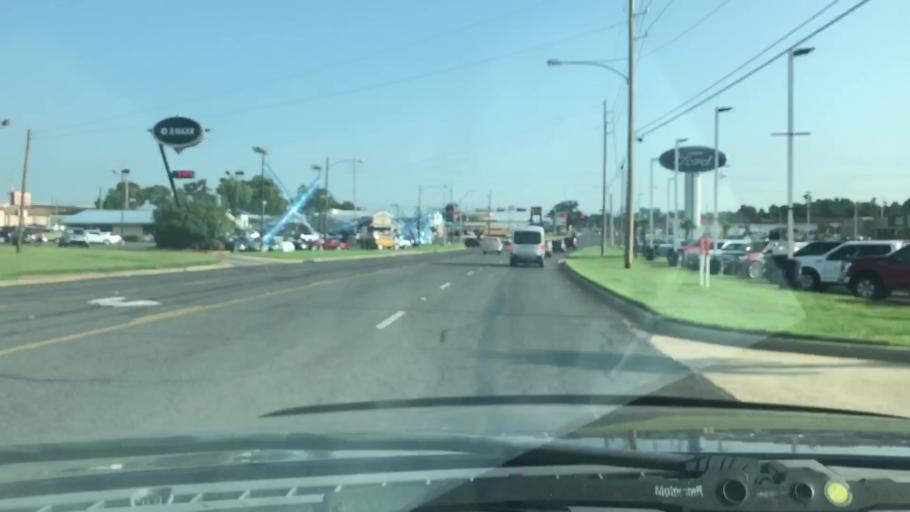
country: US
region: Arkansas
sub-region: Miller County
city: Texarkana
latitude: 33.4475
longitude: -94.0655
